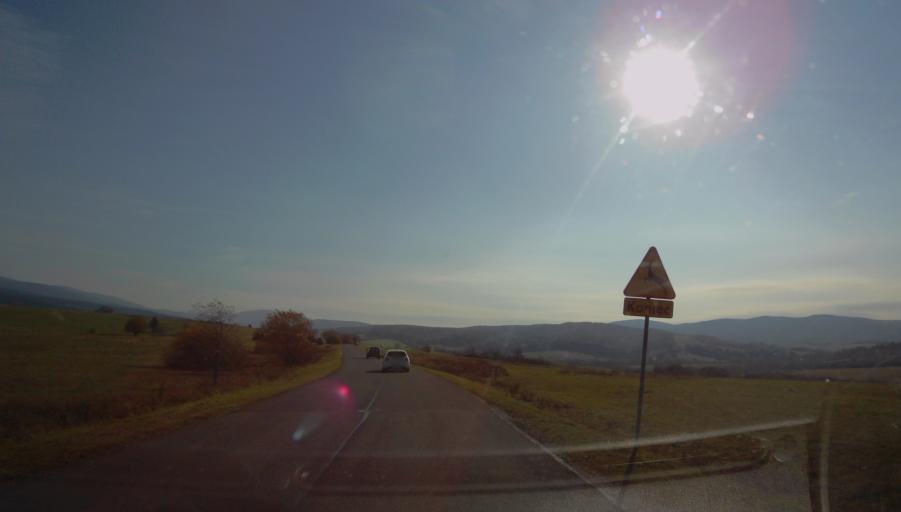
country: PL
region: Subcarpathian Voivodeship
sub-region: Powiat sanocki
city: Komancza
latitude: 49.2529
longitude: 22.0978
